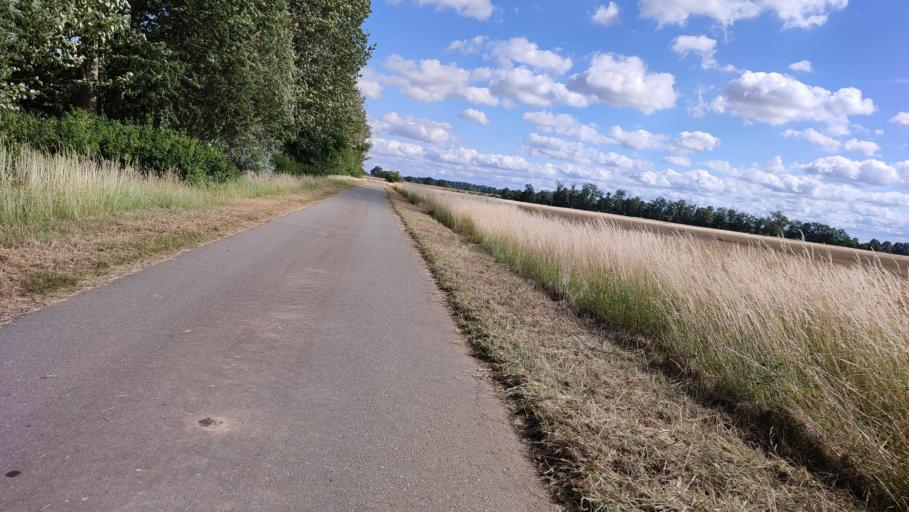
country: DE
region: Lower Saxony
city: Damnatz
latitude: 53.1825
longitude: 11.1464
